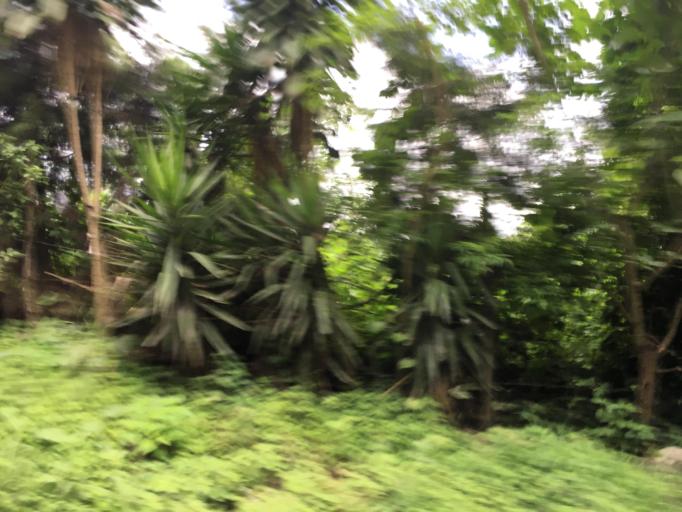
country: GT
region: Guatemala
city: Villa Canales
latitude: 14.4356
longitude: -90.5351
